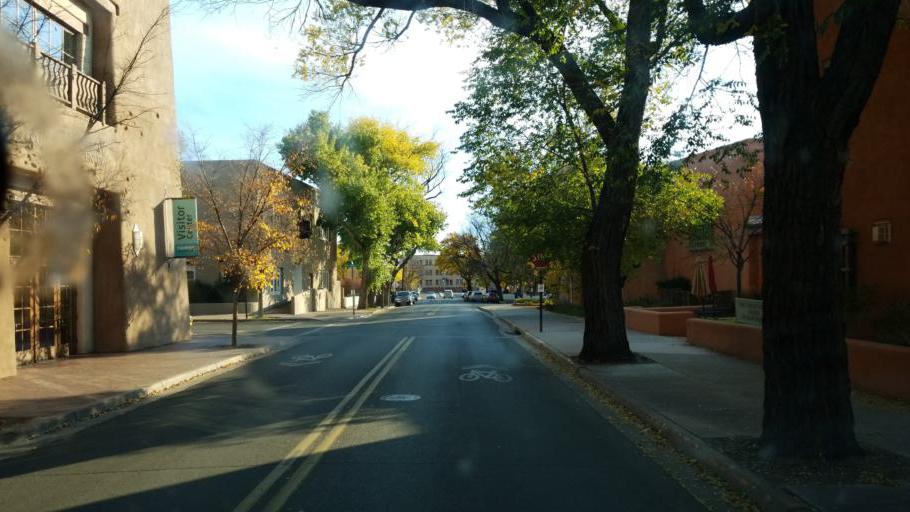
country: US
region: New Mexico
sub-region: Santa Fe County
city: Santa Fe
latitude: 35.6902
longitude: -105.9402
